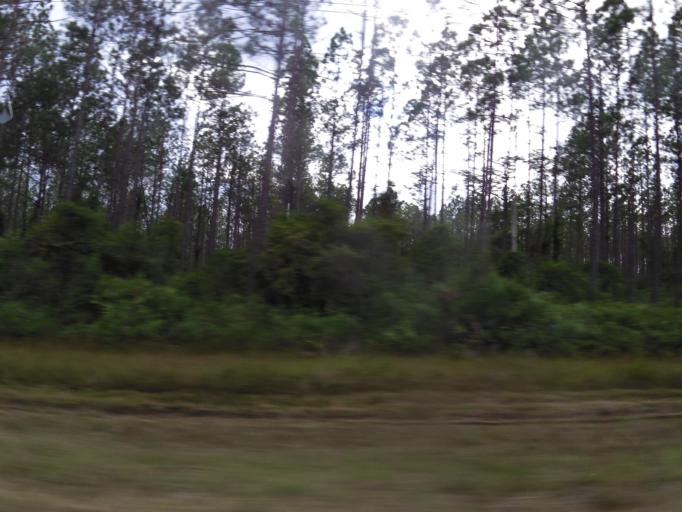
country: US
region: Florida
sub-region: Nassau County
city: Hilliard
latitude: 30.5853
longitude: -82.0471
